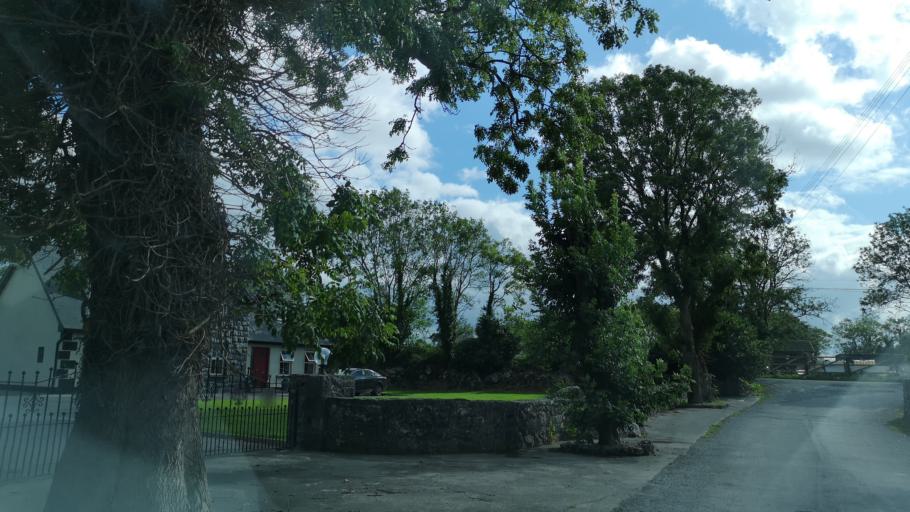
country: IE
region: Connaught
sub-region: County Galway
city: Moycullen
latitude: 53.3537
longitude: -9.1596
